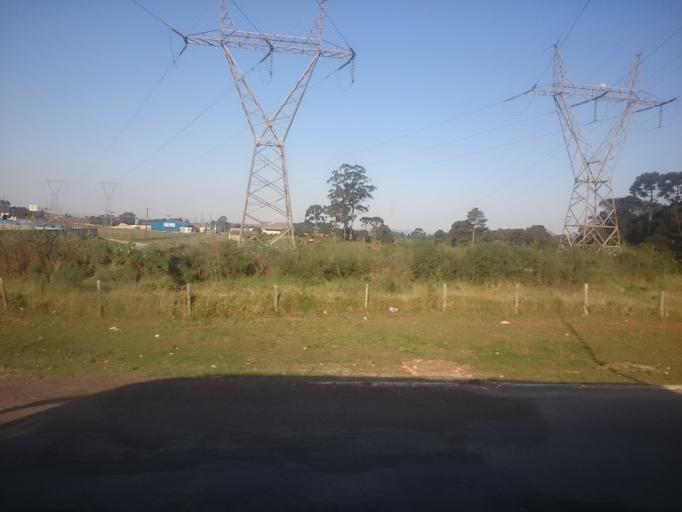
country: BR
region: Parana
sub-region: Araucaria
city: Araucaria
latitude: -25.5943
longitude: -49.3160
